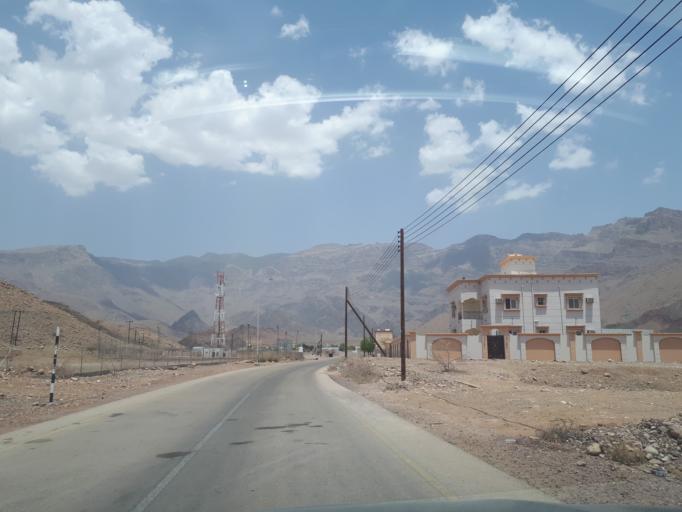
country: OM
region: Ash Sharqiyah
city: Badiyah
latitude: 22.4760
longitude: 59.1202
